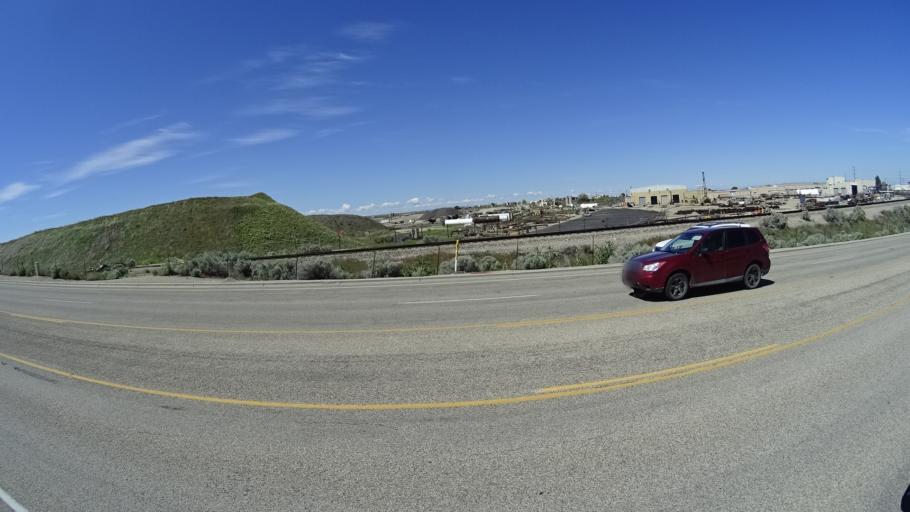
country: US
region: Idaho
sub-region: Ada County
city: Boise
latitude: 43.5574
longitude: -116.1639
